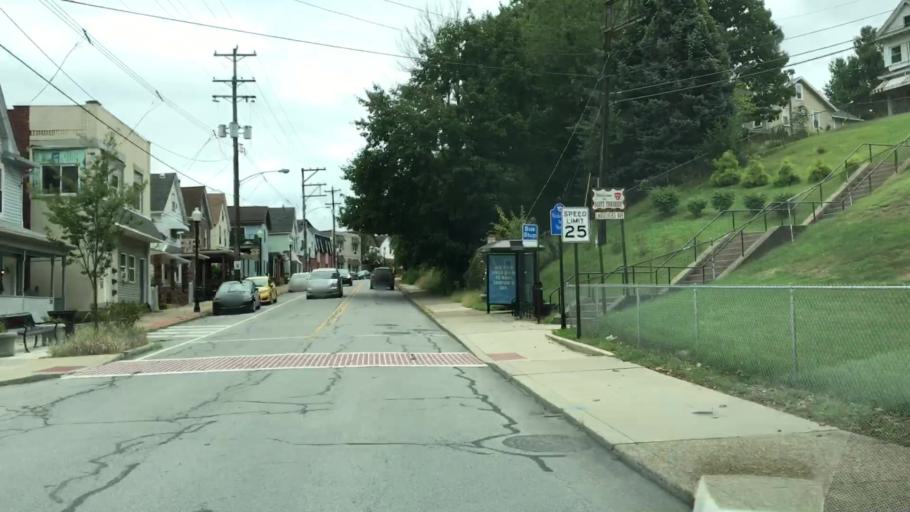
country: US
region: Pennsylvania
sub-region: Allegheny County
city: Carnegie
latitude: 40.4019
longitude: -80.0885
